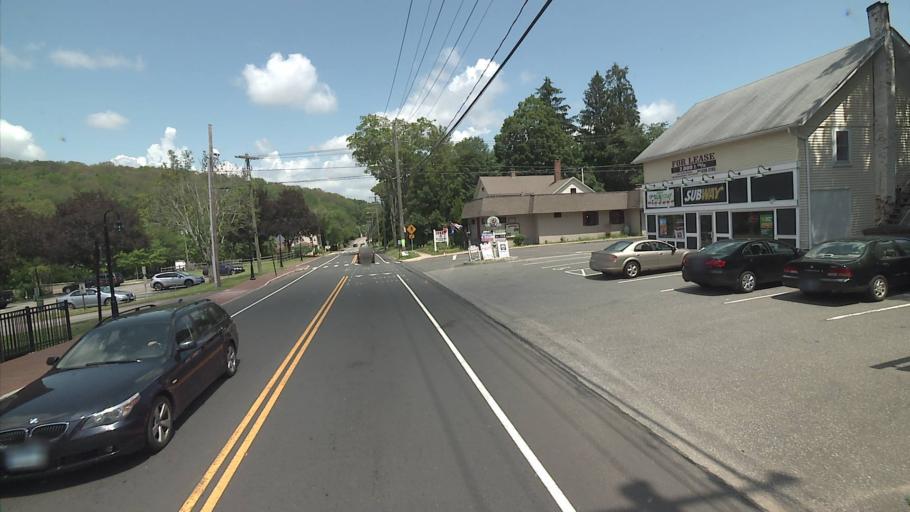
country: US
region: Connecticut
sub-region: Middlesex County
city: Deep River Center
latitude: 41.3909
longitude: -72.4381
